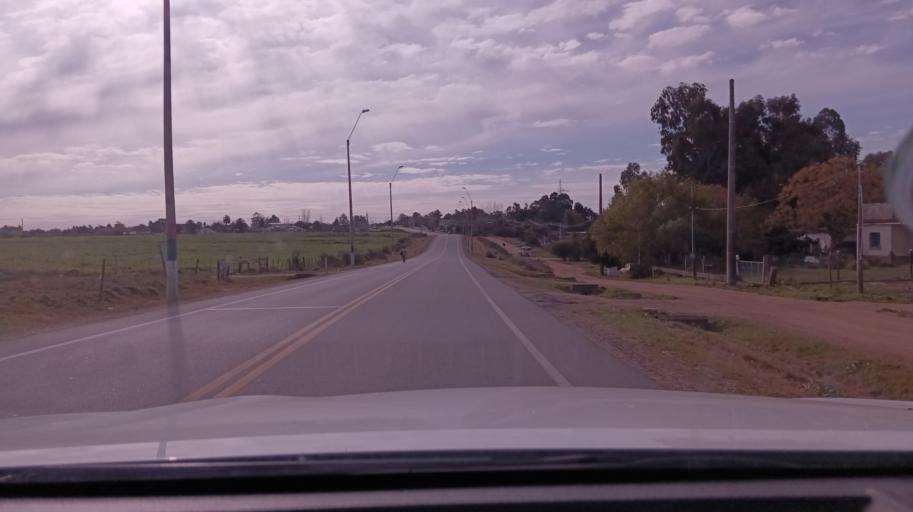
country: UY
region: Canelones
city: Toledo
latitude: -34.7451
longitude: -56.1120
